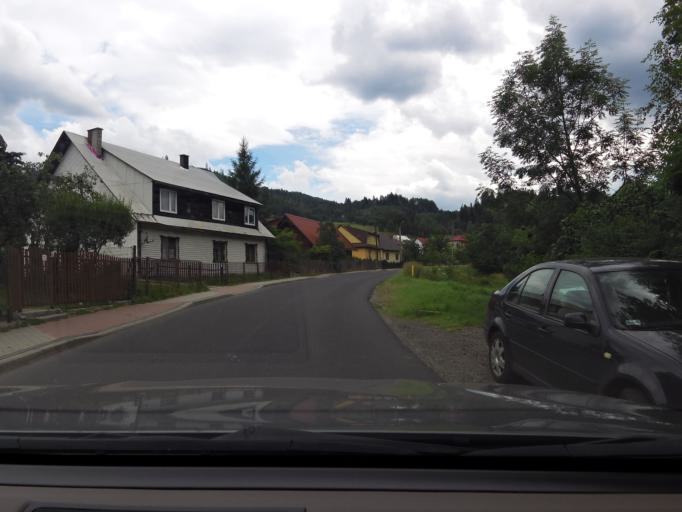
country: PL
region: Silesian Voivodeship
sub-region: Powiat zywiecki
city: Ujsoly
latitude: 49.4747
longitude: 19.1470
